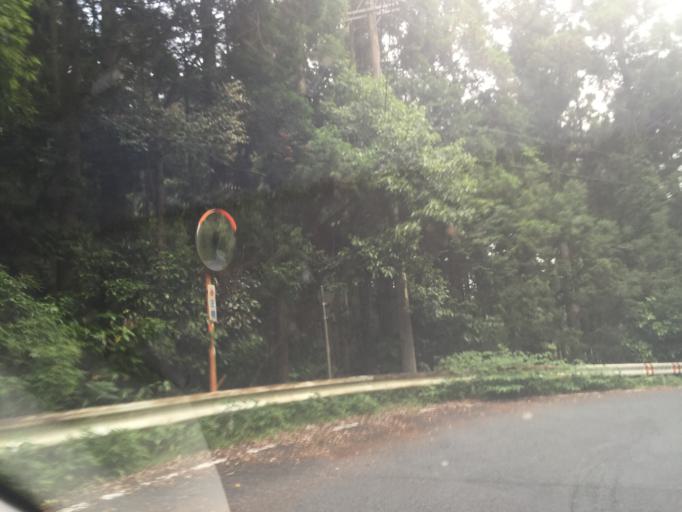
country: JP
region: Shizuoka
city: Kakegawa
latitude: 34.8313
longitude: 138.0157
